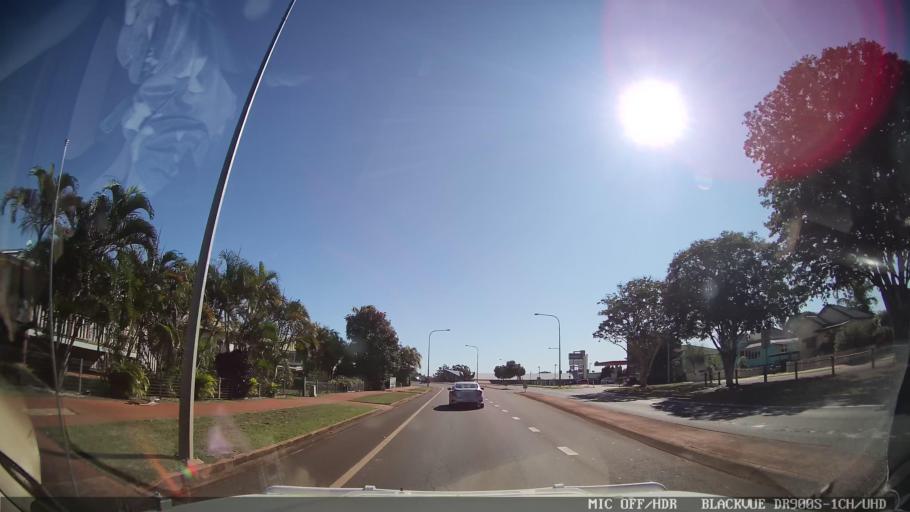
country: AU
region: Queensland
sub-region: Bundaberg
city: Childers
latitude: -25.2331
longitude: 152.2719
